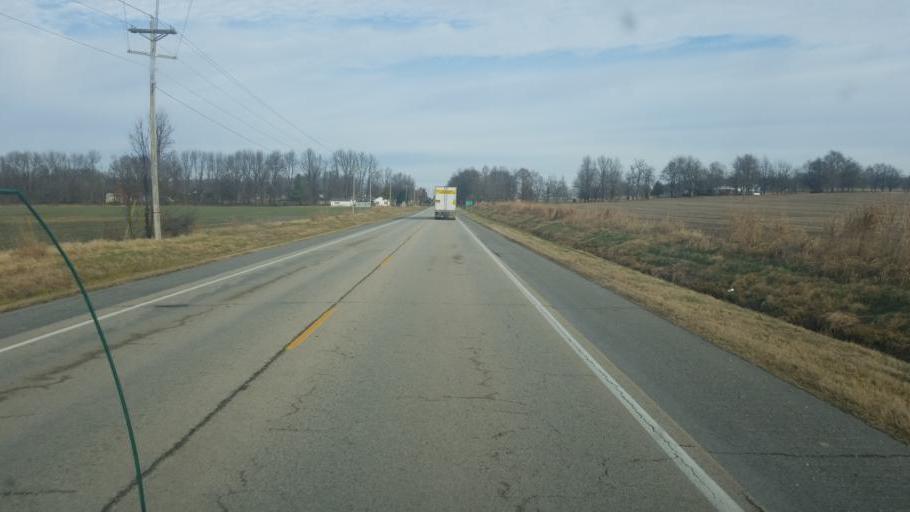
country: US
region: Missouri
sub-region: Stoddard County
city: Bloomfield
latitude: 36.9014
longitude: -89.9227
